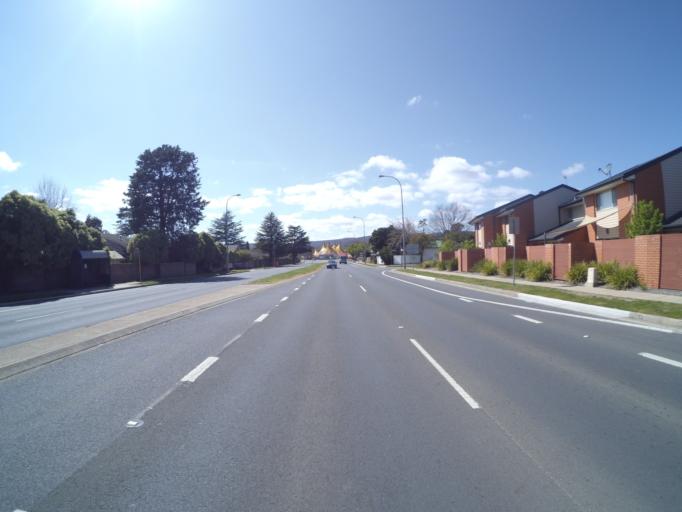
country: AU
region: New South Wales
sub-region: Queanbeyan
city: Queanbeyan
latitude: -35.3567
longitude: 149.2262
